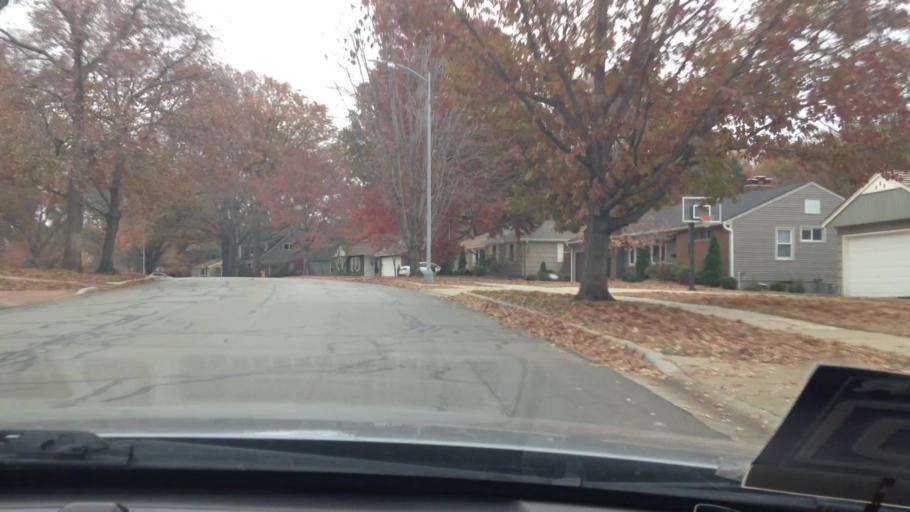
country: US
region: Kansas
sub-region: Johnson County
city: Prairie Village
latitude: 38.9998
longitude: -94.6245
